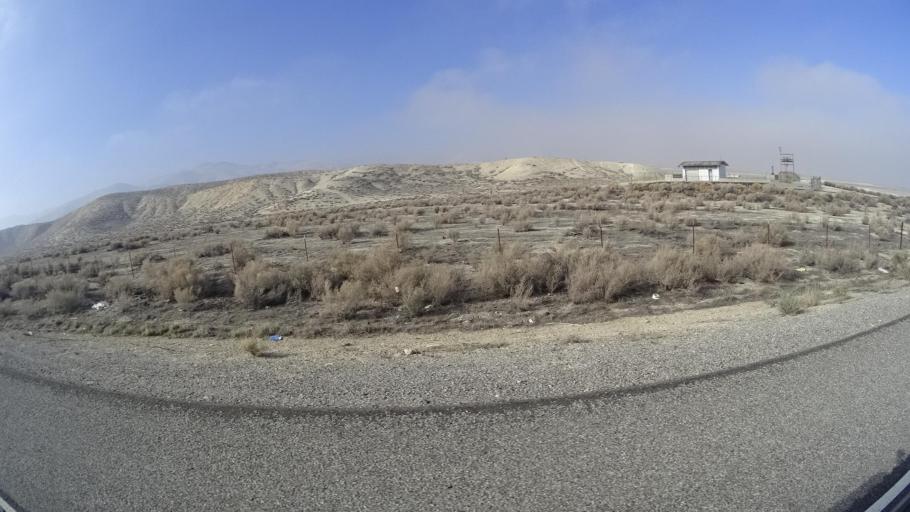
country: US
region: California
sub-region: Kern County
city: Maricopa
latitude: 35.0421
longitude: -119.4246
